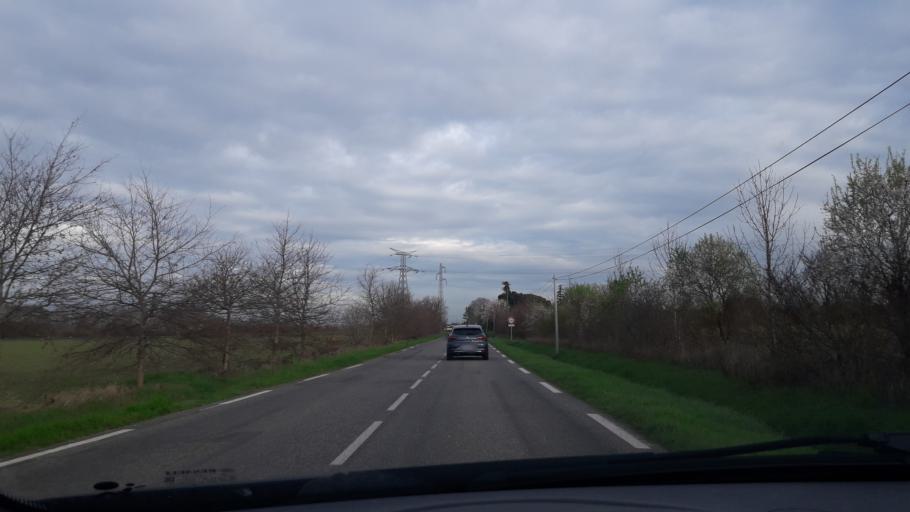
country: FR
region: Midi-Pyrenees
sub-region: Departement de la Haute-Garonne
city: Ondes
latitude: 43.8017
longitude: 1.2928
